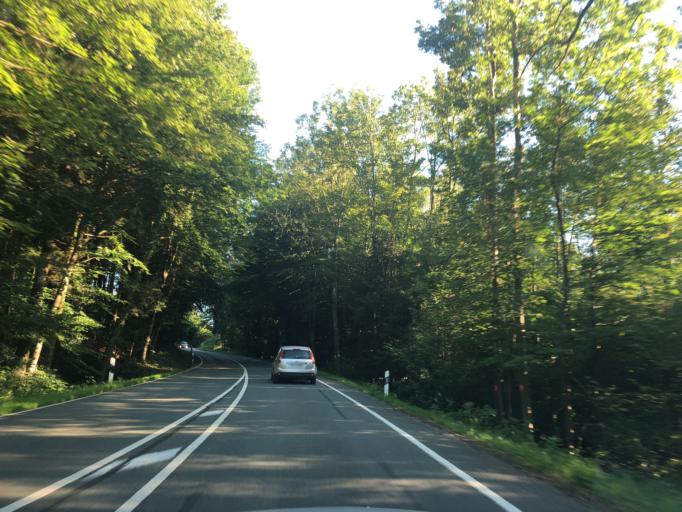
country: DE
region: Bavaria
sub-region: Upper Bavaria
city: Riedering
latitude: 47.8606
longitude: 12.2408
